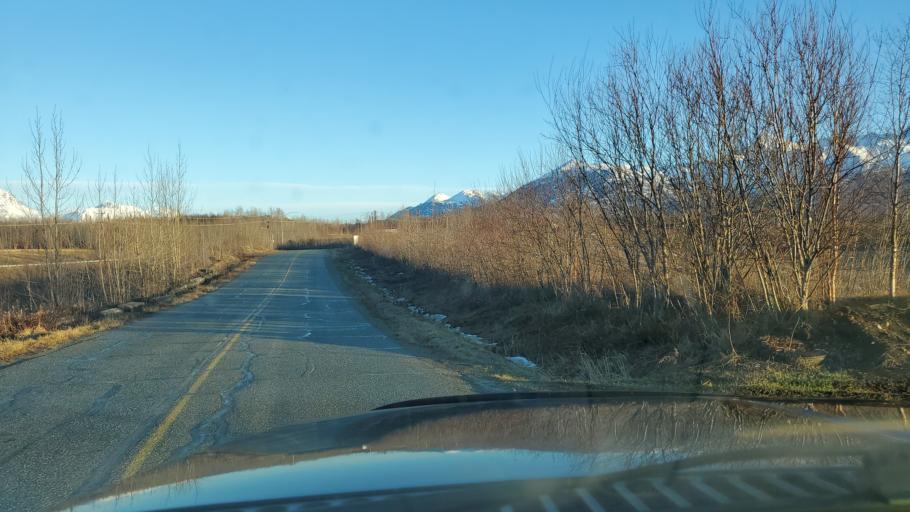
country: US
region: Alaska
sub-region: Matanuska-Susitna Borough
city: Palmer
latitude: 61.5980
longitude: -149.1402
